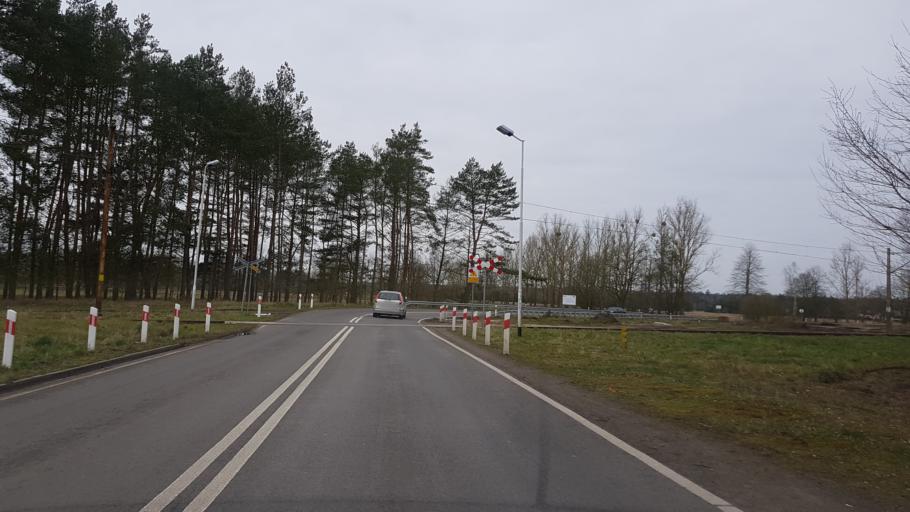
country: PL
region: West Pomeranian Voivodeship
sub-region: Powiat policki
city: Police
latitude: 53.6202
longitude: 14.5048
